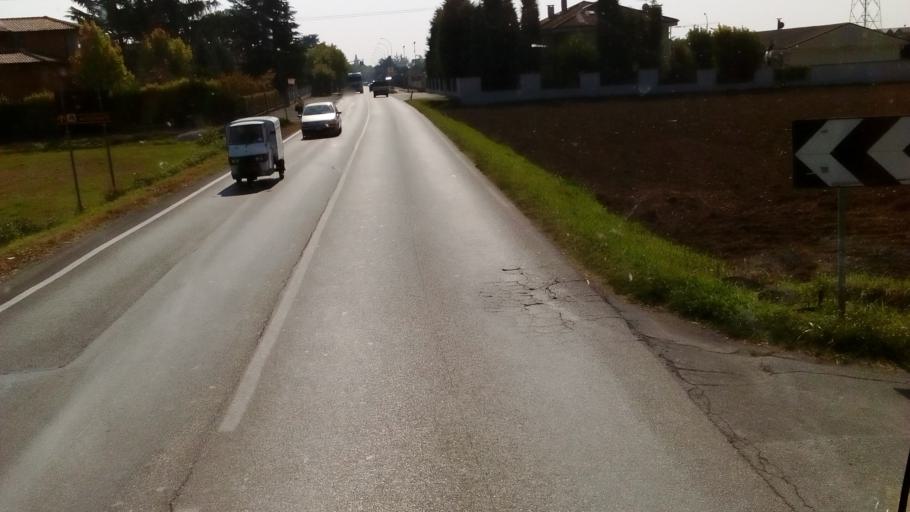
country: IT
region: Lombardy
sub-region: Provincia di Bergamo
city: Urgnano
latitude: 45.5896
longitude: 9.7024
